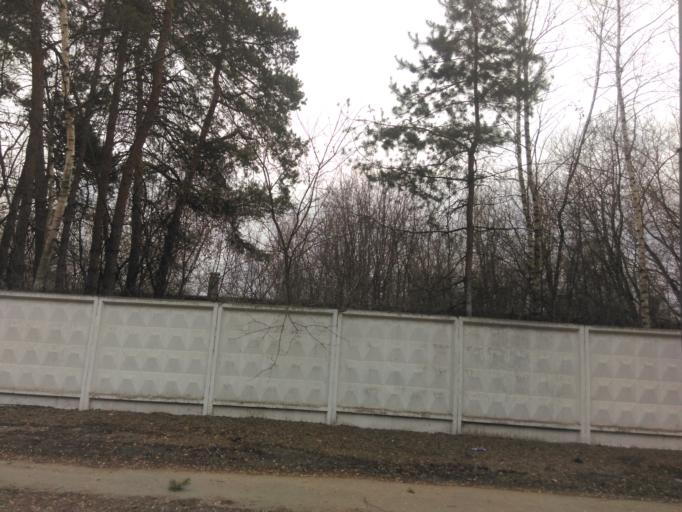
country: RU
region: Moskovskaya
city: Gorki Vtoryye
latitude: 55.7233
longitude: 37.1707
